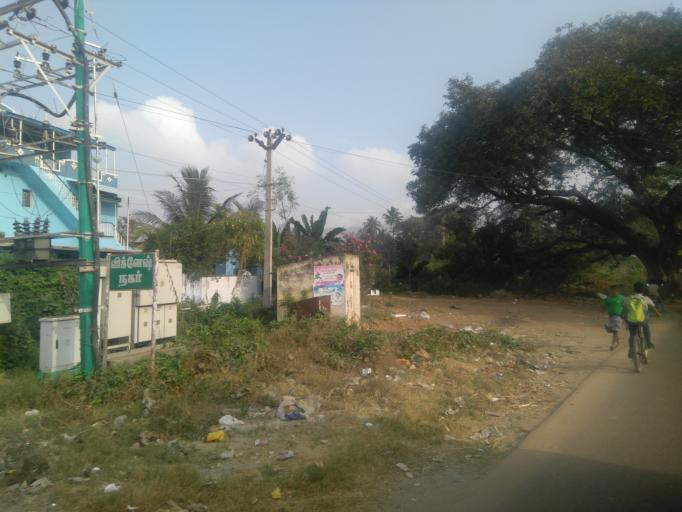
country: IN
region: Tamil Nadu
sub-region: Coimbatore
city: Perur
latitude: 11.0381
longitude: 76.8916
